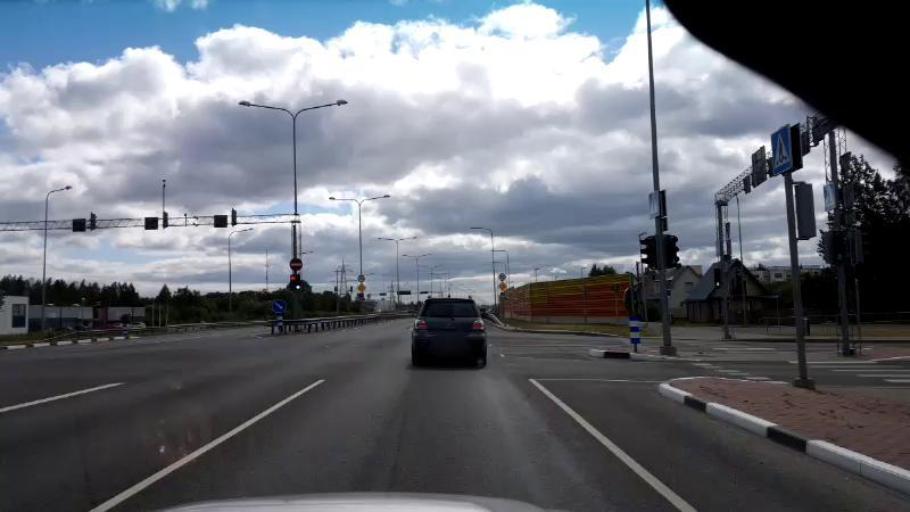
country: EE
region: Paernumaa
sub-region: Paernu linn
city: Parnu
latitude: 58.3983
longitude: 24.5186
